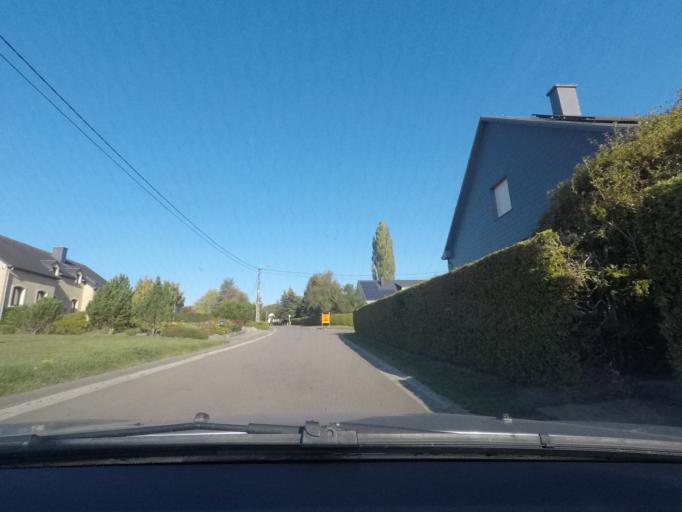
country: BE
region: Wallonia
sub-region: Province du Luxembourg
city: Messancy
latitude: 49.6330
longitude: 5.7940
